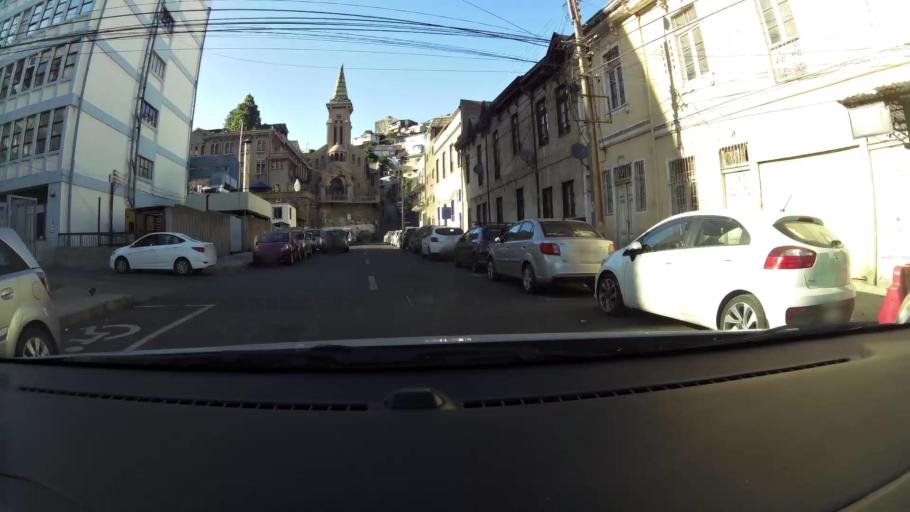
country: CL
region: Valparaiso
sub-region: Provincia de Valparaiso
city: Valparaiso
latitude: -33.0511
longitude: -71.6112
